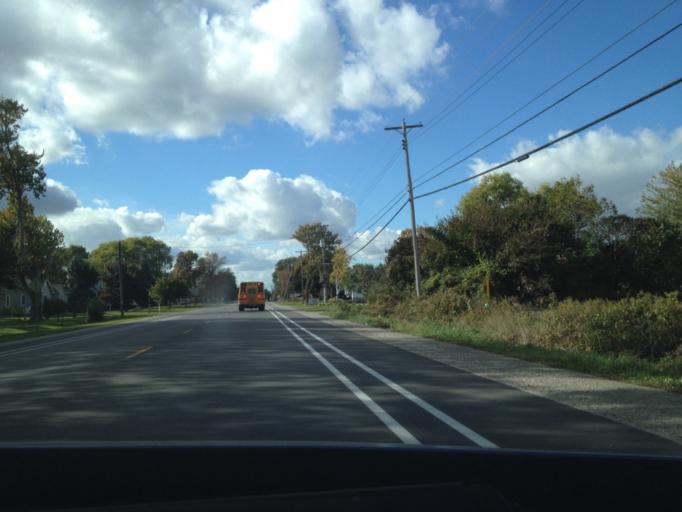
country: CA
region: Ontario
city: Amherstburg
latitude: 42.0360
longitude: -82.7067
